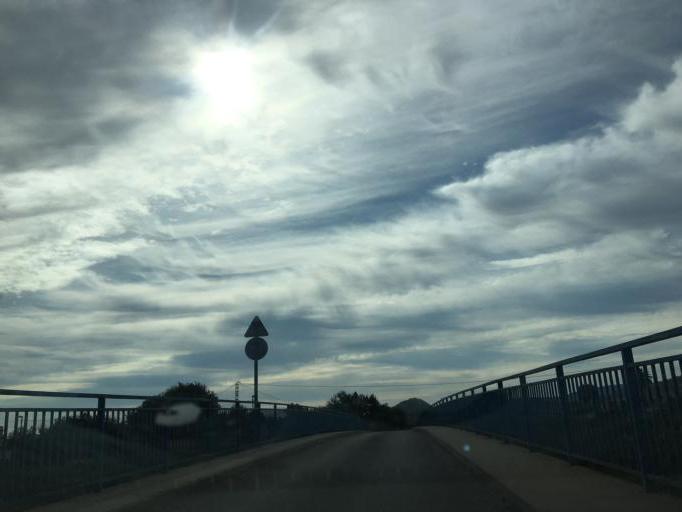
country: ES
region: Murcia
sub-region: Murcia
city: Santomera
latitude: 38.0127
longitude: -1.0443
